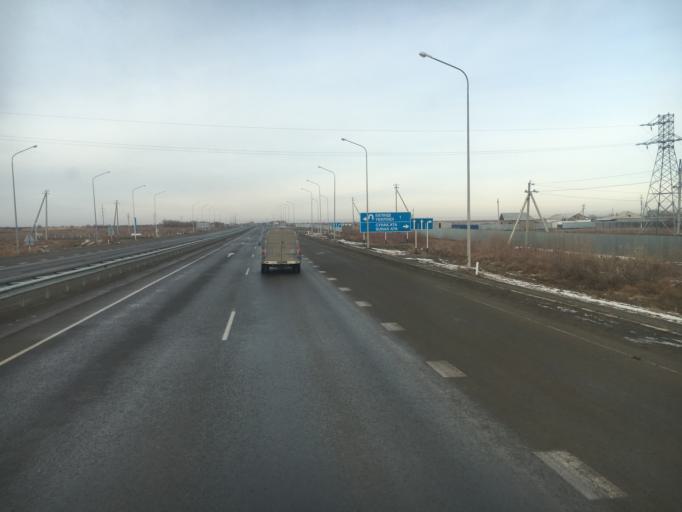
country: KZ
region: Qyzylorda
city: Shieli
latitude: 44.1391
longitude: 66.9663
